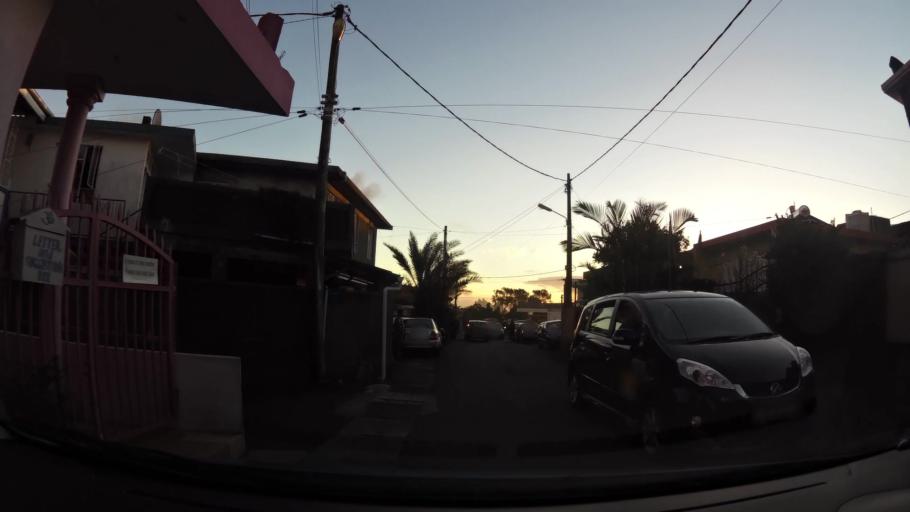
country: MU
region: Plaines Wilhems
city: Curepipe
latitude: -20.3019
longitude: 57.5245
